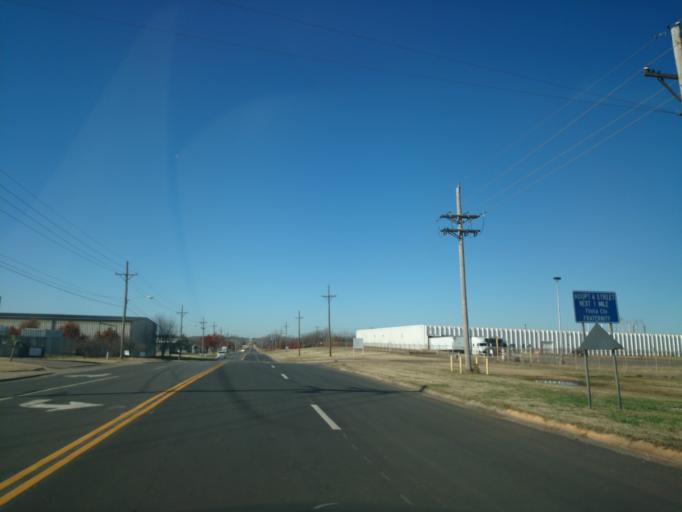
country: US
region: Oklahoma
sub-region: Payne County
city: Stillwater
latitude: 36.1595
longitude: -97.0519
